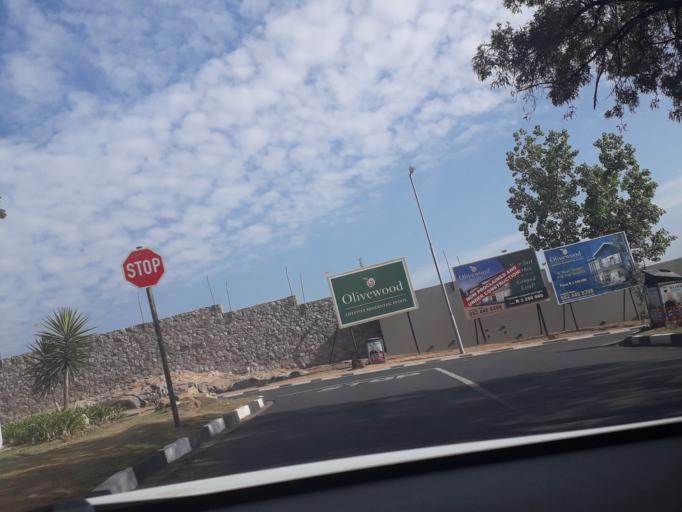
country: ZA
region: Gauteng
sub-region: City of Johannesburg Metropolitan Municipality
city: Diepsloot
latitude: -26.0521
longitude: 27.9824
